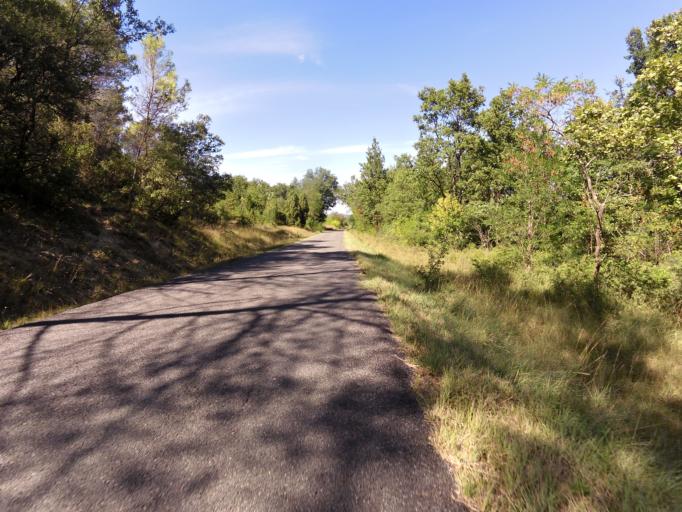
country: FR
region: Languedoc-Roussillon
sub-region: Departement du Gard
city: Quissac
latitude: 43.9465
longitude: 4.0493
